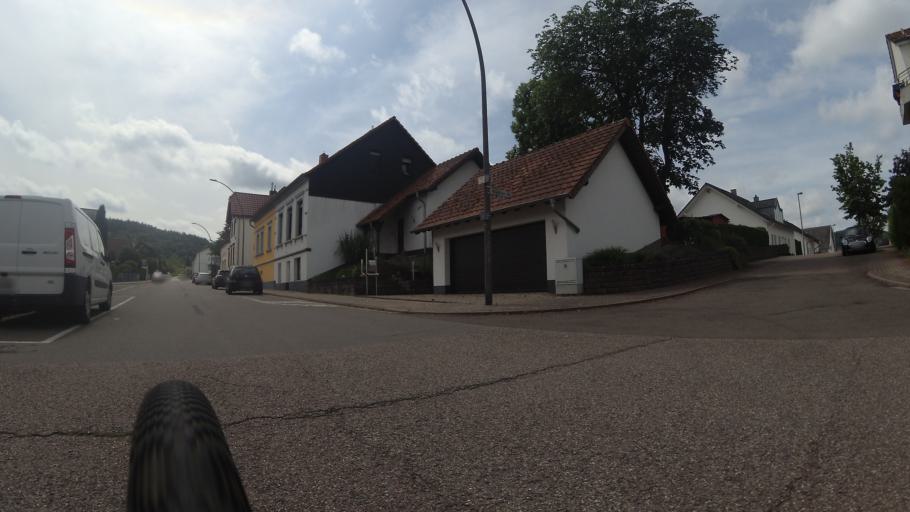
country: DE
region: Saarland
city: Sankt Ingbert
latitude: 49.2728
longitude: 7.1335
